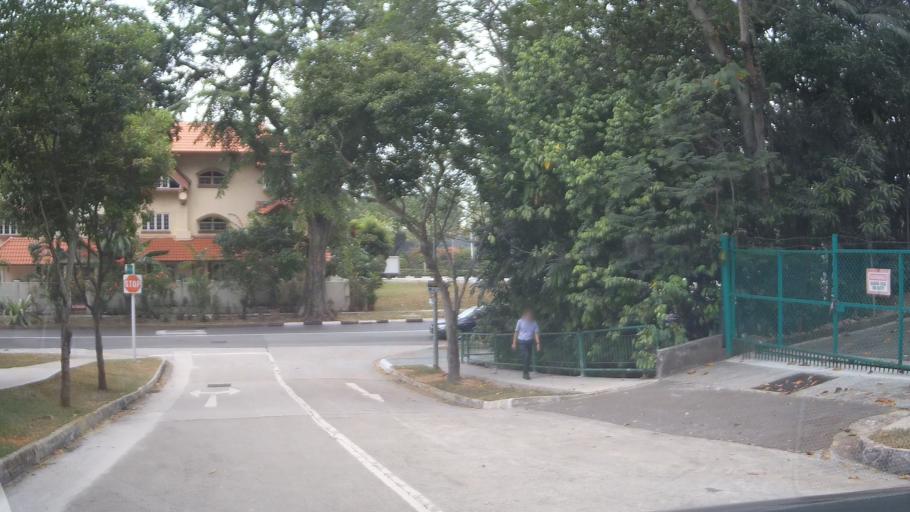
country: SG
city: Singapore
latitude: 1.2827
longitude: 103.7828
